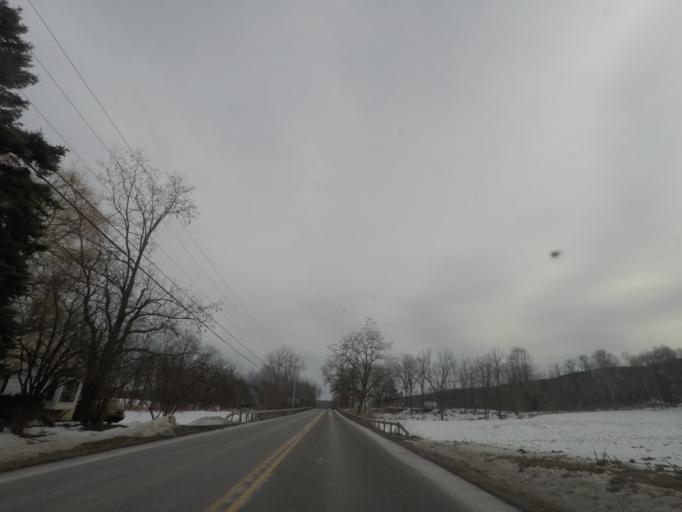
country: US
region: New York
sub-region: Albany County
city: Voorheesville
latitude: 42.5852
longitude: -73.9830
